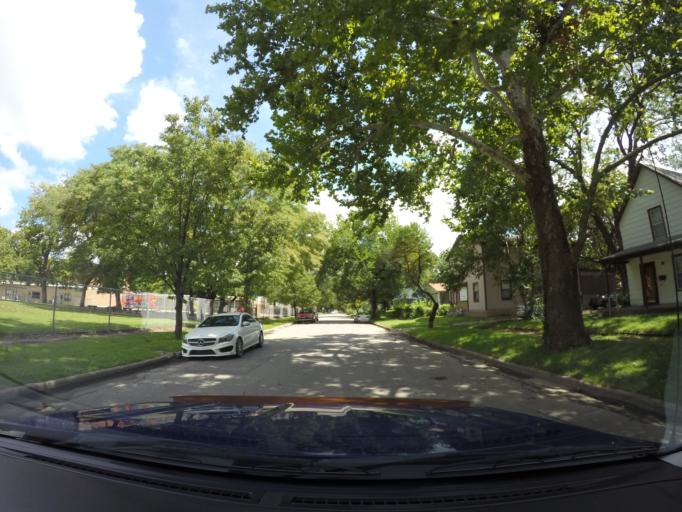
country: US
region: Kansas
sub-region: Riley County
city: Manhattan
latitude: 39.1763
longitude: -96.5680
